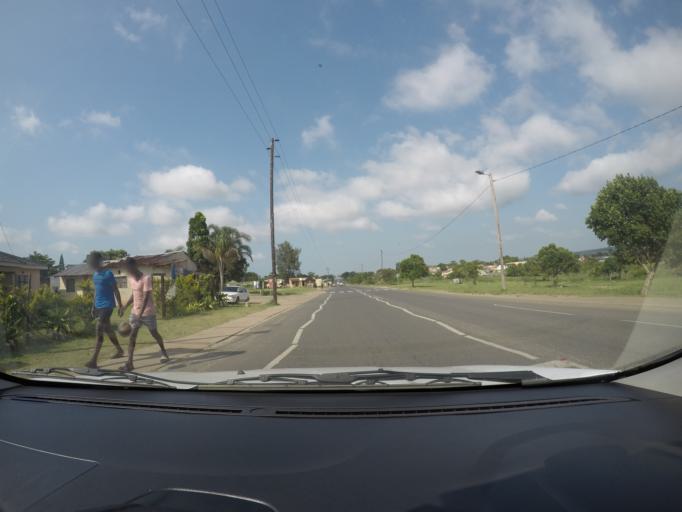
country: ZA
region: KwaZulu-Natal
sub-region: uThungulu District Municipality
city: eSikhawini
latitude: -28.8756
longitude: 31.9152
